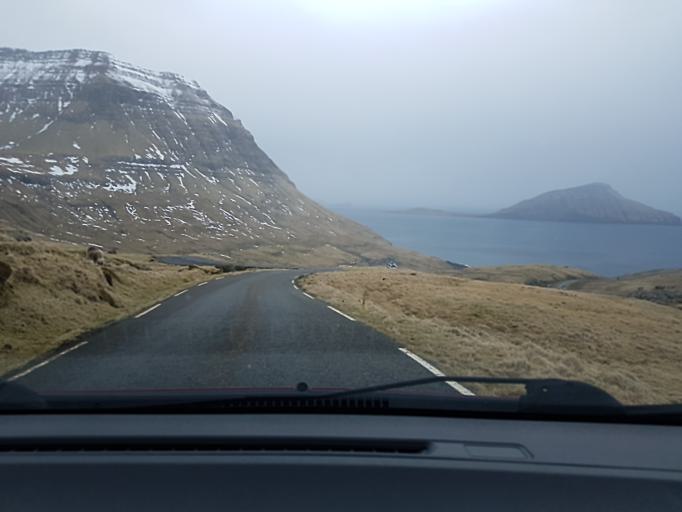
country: FO
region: Streymoy
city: Kollafjordhur
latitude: 62.0486
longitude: -6.9230
